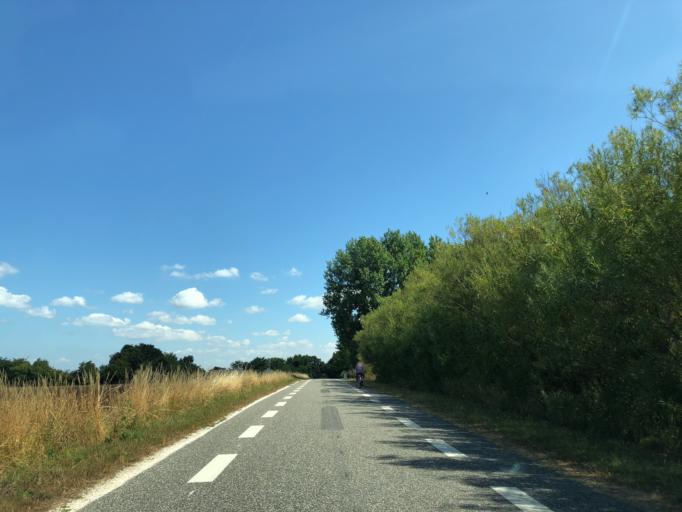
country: DK
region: Capital Region
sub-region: Halsnaes Kommune
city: Liseleje
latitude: 55.9771
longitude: 11.9178
